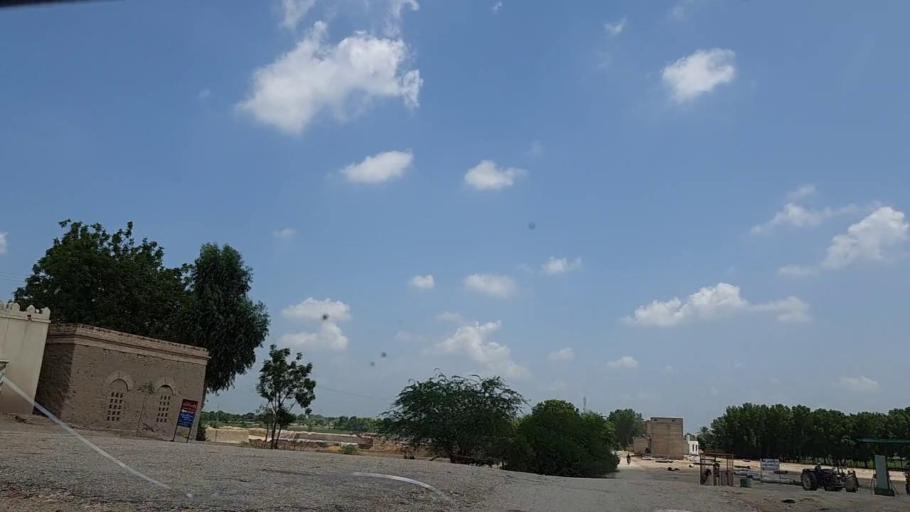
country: PK
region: Sindh
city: Tharu Shah
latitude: 26.9933
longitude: 68.0719
